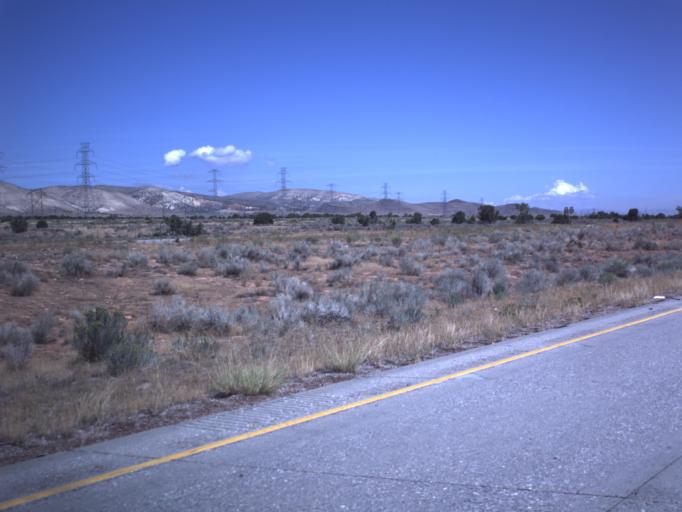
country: US
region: Utah
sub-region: Sevier County
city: Aurora
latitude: 38.8622
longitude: -111.9817
